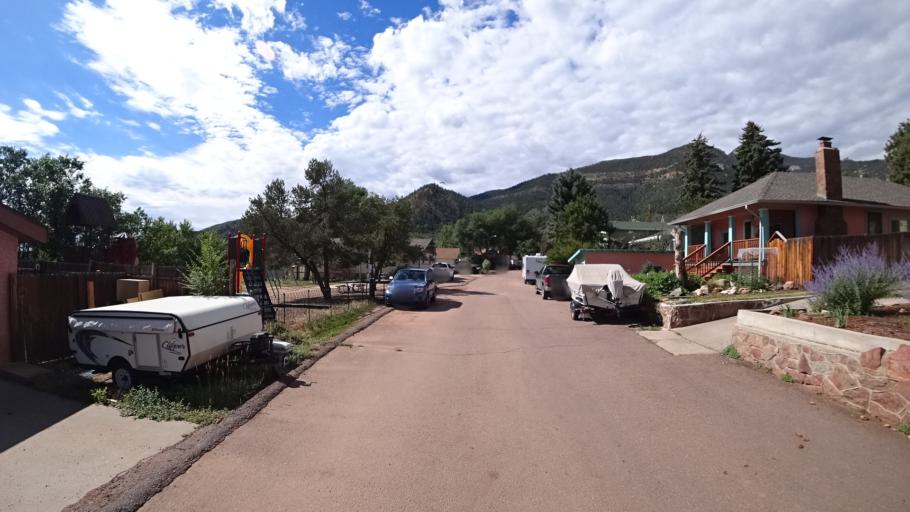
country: US
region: Colorado
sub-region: El Paso County
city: Manitou Springs
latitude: 38.8614
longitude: -104.9231
